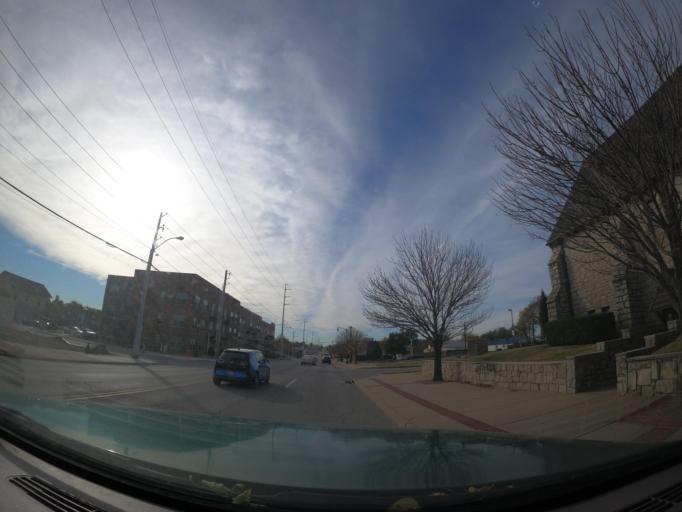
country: US
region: Oklahoma
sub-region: Tulsa County
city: Tulsa
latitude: 36.1530
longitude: -95.9582
